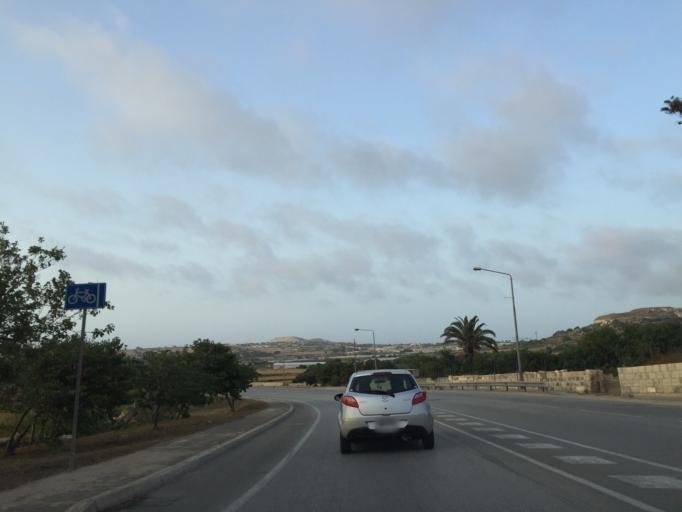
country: MT
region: Il-Mosta
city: Mosta
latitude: 35.9192
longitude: 14.4146
